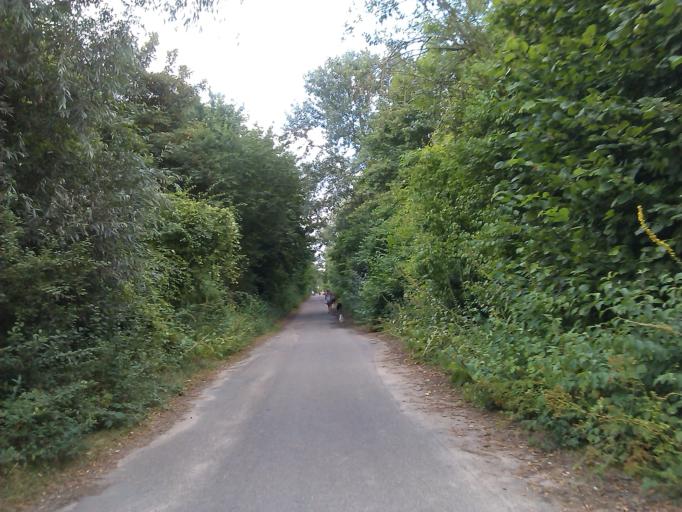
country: DE
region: Rheinland-Pfalz
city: Otterstadt
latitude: 49.3628
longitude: 8.4600
